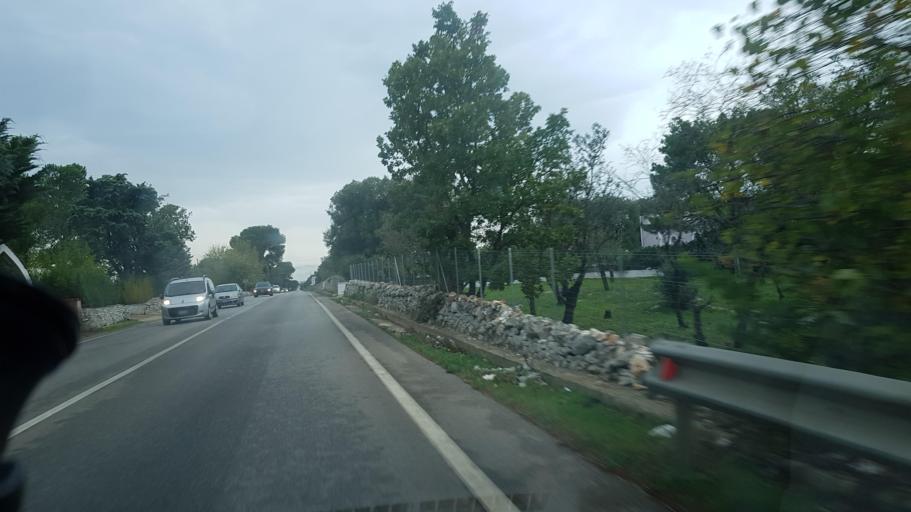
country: IT
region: Apulia
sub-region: Provincia di Brindisi
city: Carovigno
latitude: 40.7099
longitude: 17.6388
